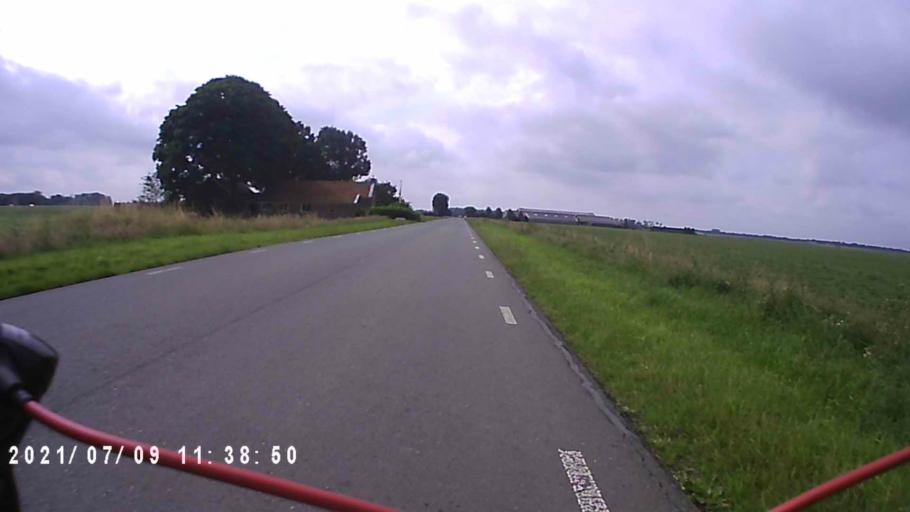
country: NL
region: Groningen
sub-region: Gemeente Slochteren
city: Slochteren
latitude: 53.2200
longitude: 6.8725
